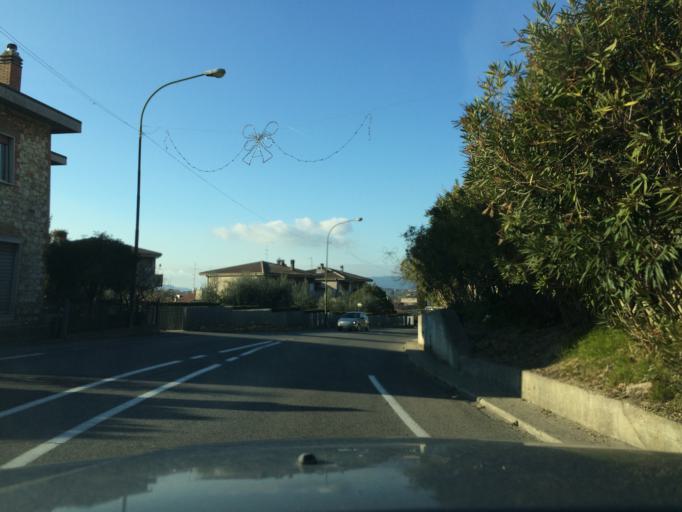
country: IT
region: Umbria
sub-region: Provincia di Terni
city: Fornole
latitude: 42.5425
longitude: 12.4557
